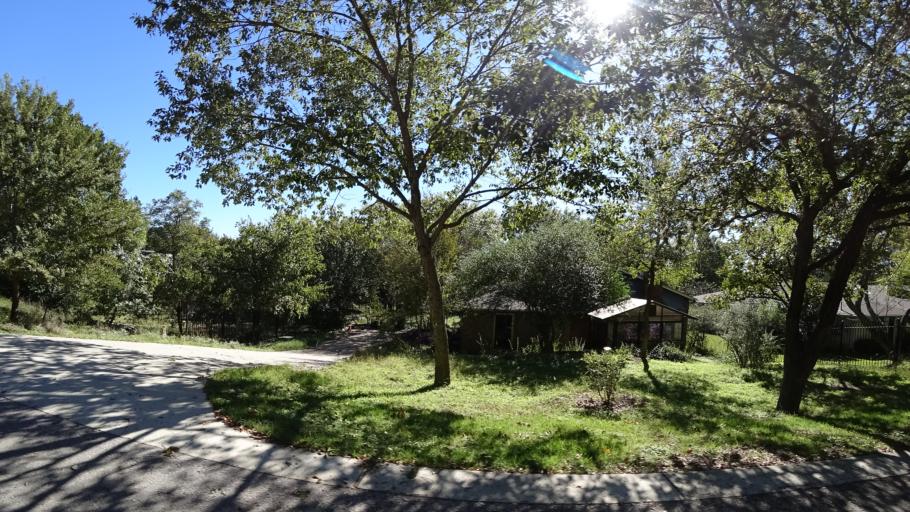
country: US
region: Texas
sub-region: Travis County
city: Rollingwood
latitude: 30.2217
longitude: -97.8116
